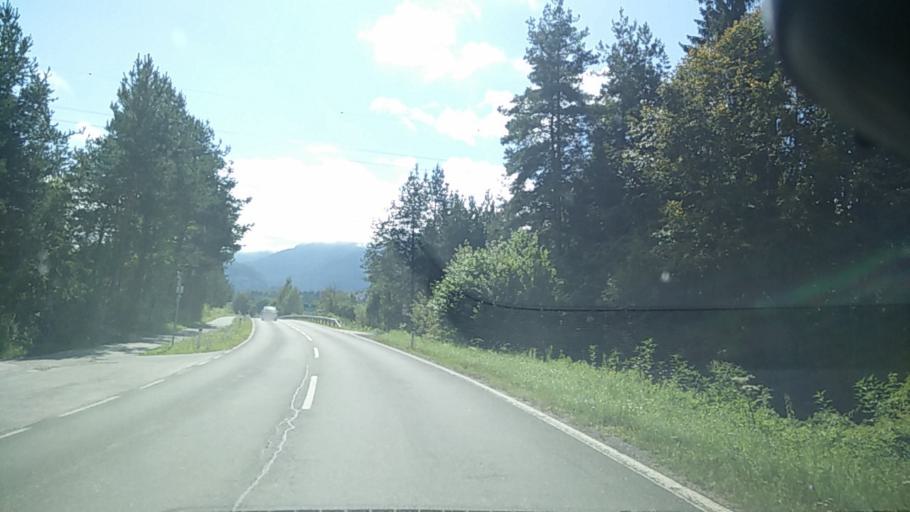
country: AT
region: Carinthia
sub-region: Politischer Bezirk Villach Land
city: Finkenstein am Faaker See
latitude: 46.5723
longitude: 13.8404
